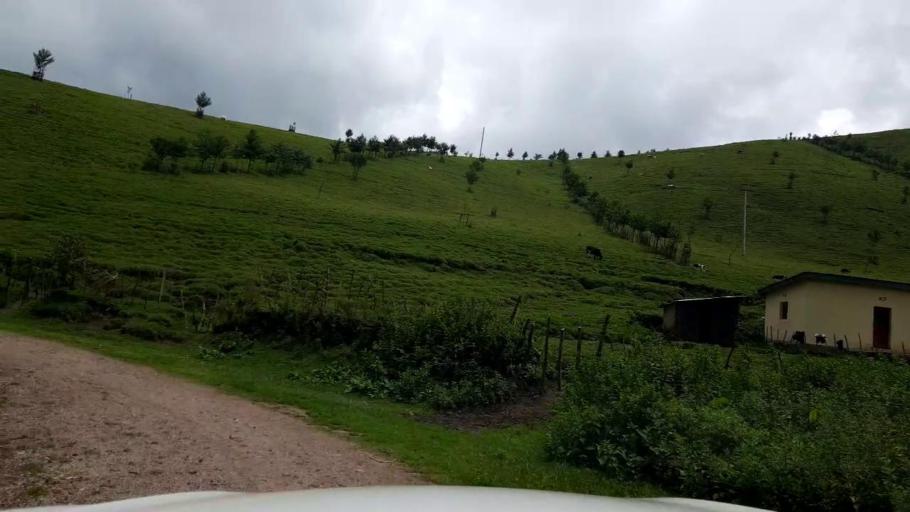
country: RW
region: Western Province
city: Gisenyi
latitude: -1.6885
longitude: 29.4228
